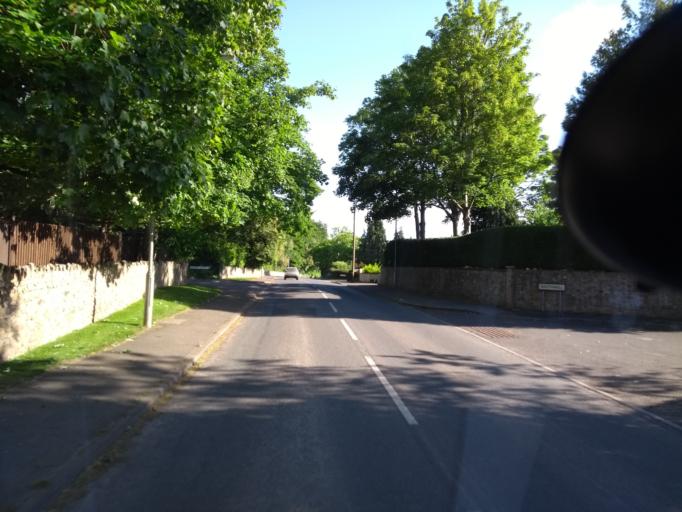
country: GB
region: England
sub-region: Somerset
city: Taunton
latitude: 50.9920
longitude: -3.1223
